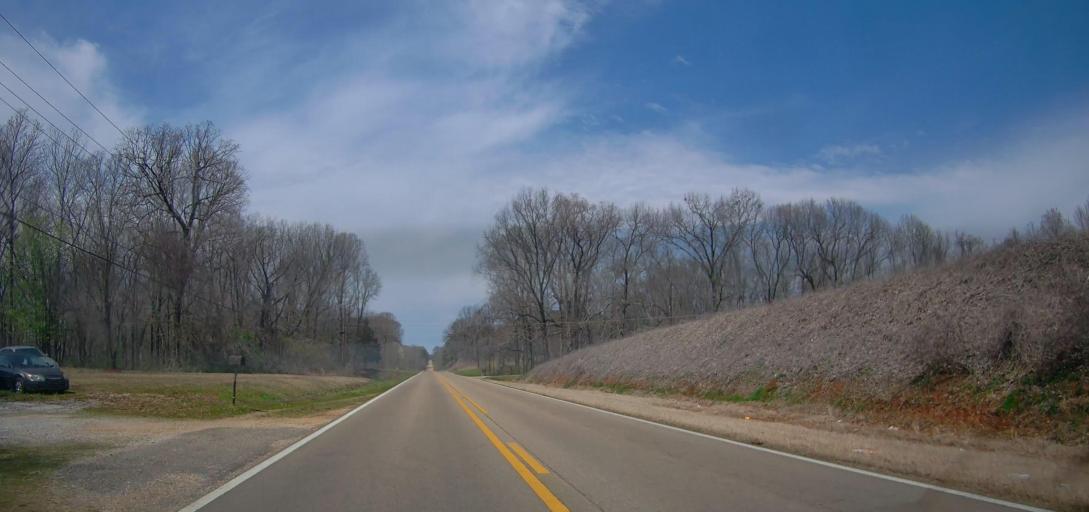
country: US
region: Mississippi
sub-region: Union County
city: New Albany
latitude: 34.4387
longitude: -88.9592
